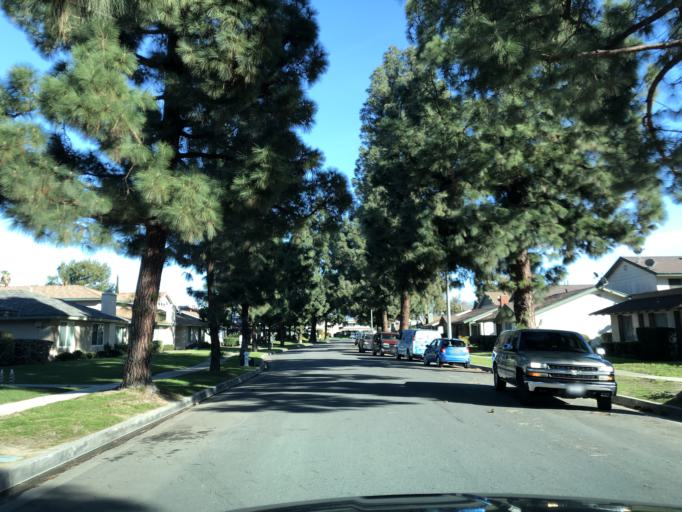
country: US
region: California
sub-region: Orange County
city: Tustin
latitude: 33.7703
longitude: -117.8337
